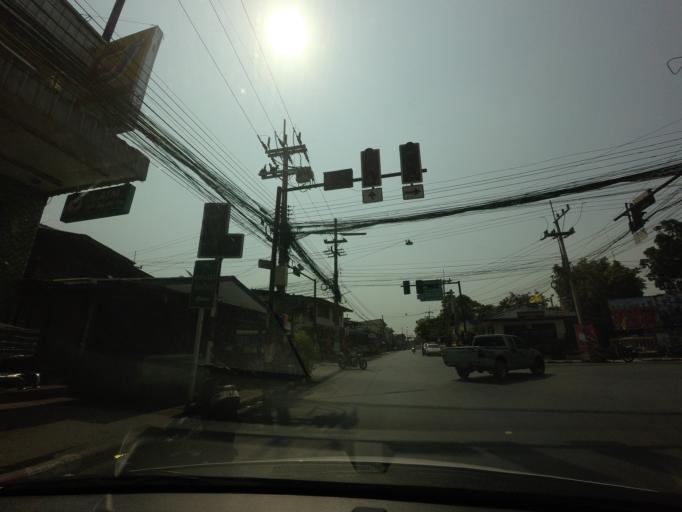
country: TH
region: Nakhon Pathom
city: Sam Phran
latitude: 13.7003
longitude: 100.2434
